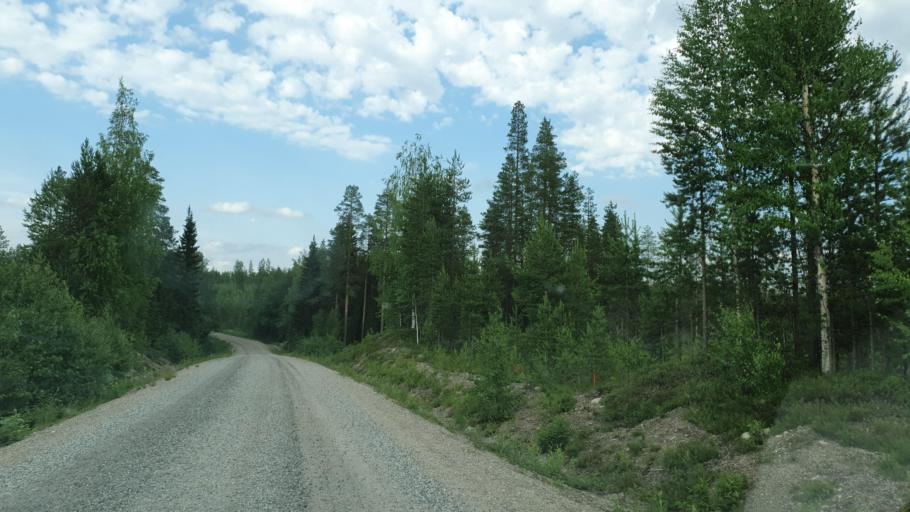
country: FI
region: Kainuu
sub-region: Kehys-Kainuu
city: Kuhmo
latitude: 64.0426
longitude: 29.8276
